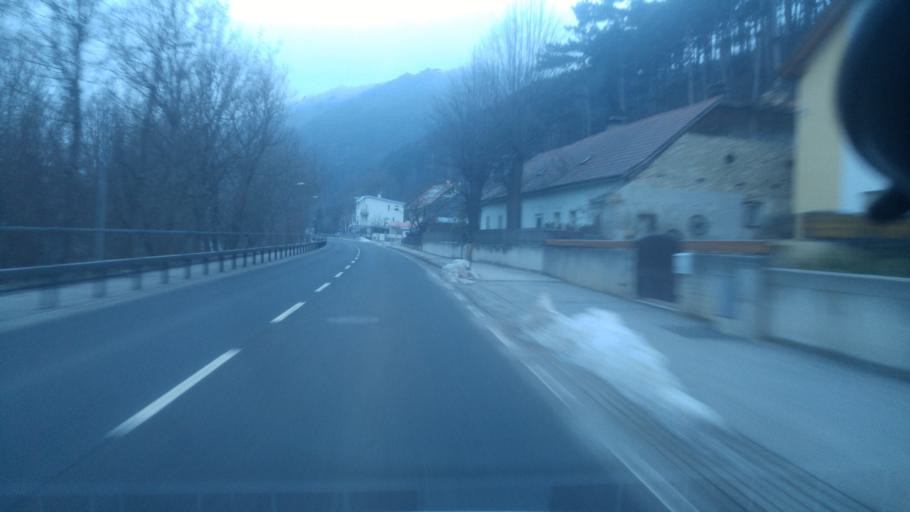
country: AT
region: Lower Austria
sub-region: Politischer Bezirk Baden
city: Weissenbach an der Triesting
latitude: 47.9818
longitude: 16.0640
